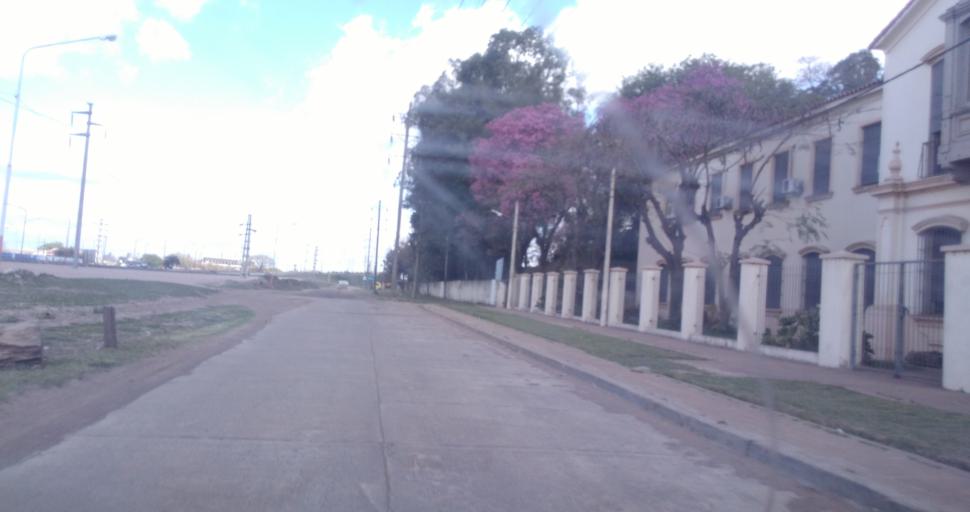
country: AR
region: Chaco
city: Fontana
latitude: -27.4315
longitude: -59.0112
